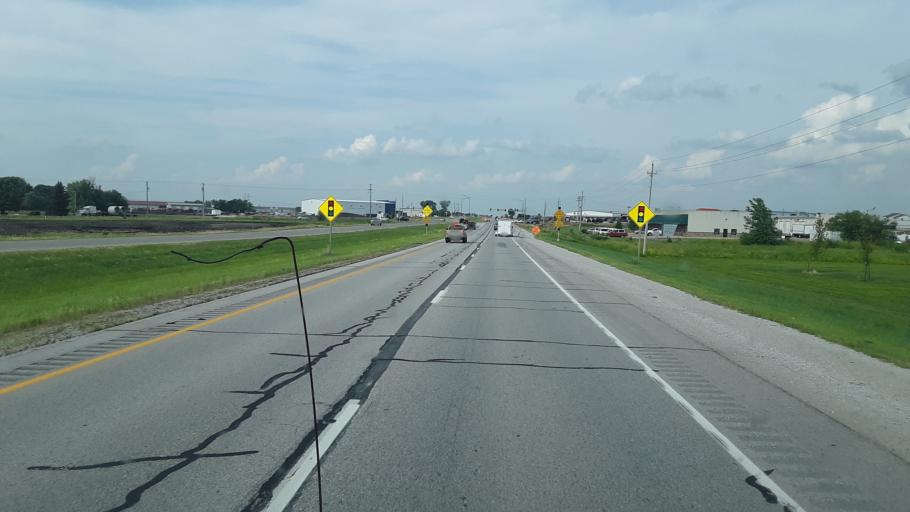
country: US
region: Iowa
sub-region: Polk County
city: Altoona
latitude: 41.6708
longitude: -93.4831
